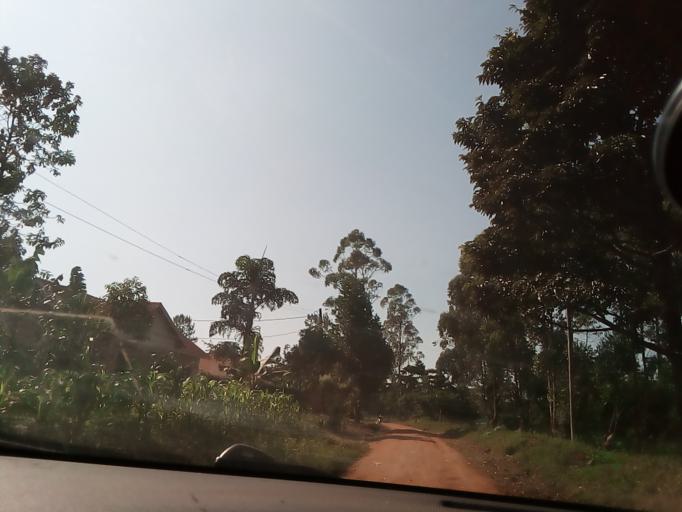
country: UG
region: Central Region
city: Masaka
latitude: -0.3393
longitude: 31.7208
